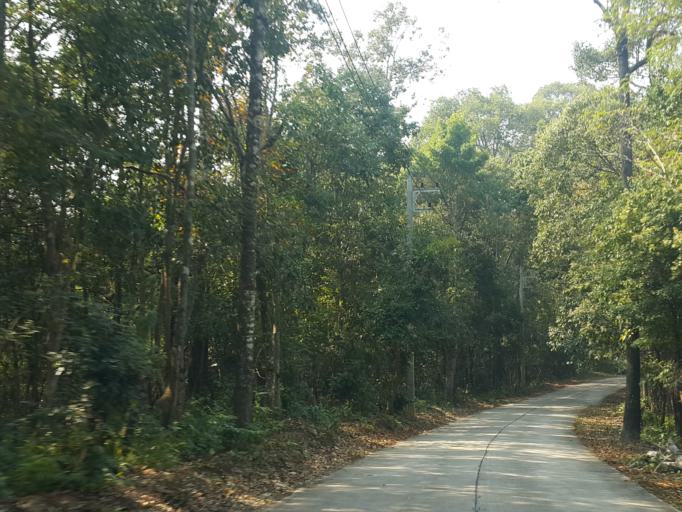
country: TH
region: Chiang Mai
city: Mae Taeng
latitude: 19.0235
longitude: 98.7888
